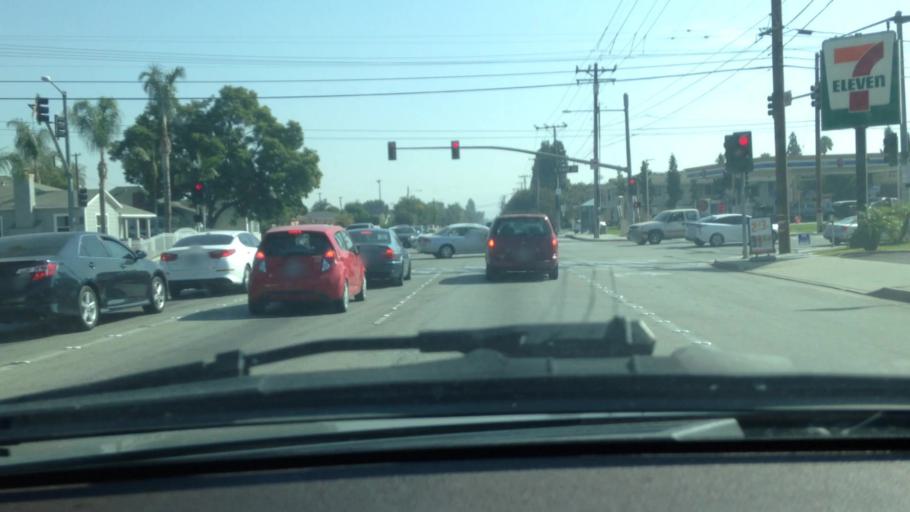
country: US
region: California
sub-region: Orange County
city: Anaheim
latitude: 33.8472
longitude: -117.9062
